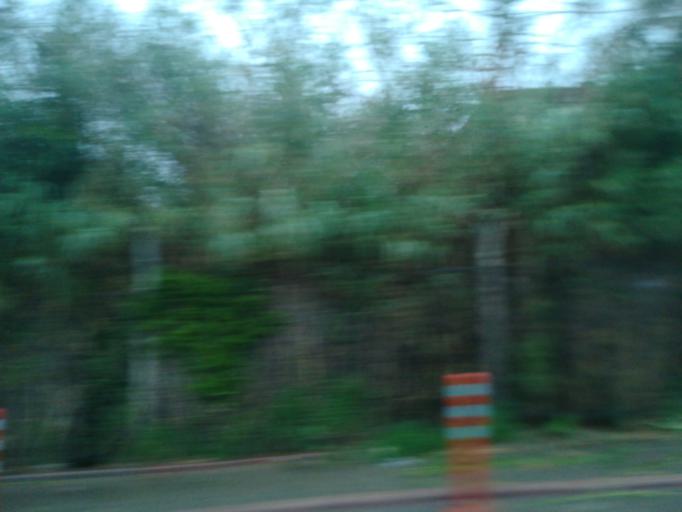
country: TR
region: Adana
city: Seyhan
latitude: 37.0063
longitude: 35.2802
